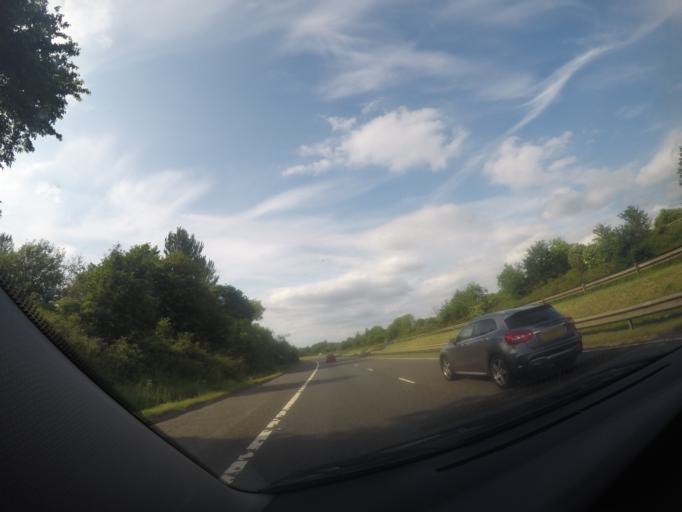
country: GB
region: Scotland
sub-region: South Lanarkshire
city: Larkhall
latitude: 55.7361
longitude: -3.9508
